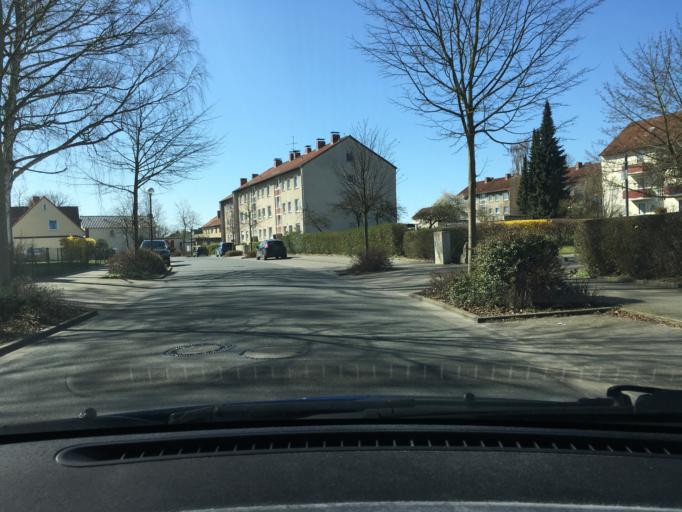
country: DE
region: Lower Saxony
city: Uelzen
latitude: 52.9652
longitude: 10.5380
